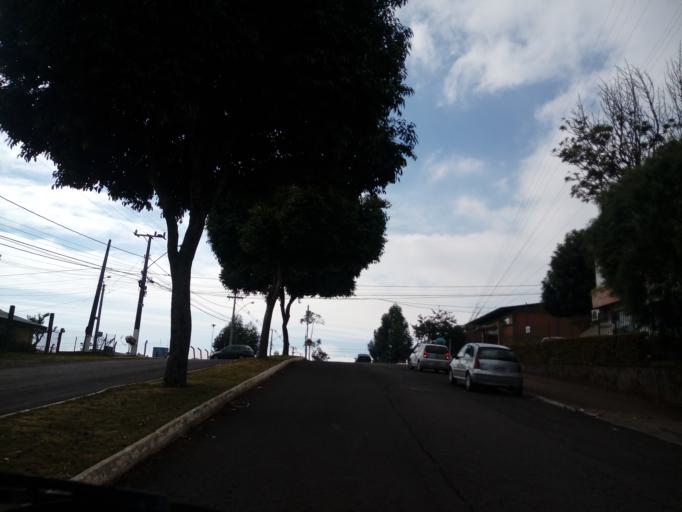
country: BR
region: Santa Catarina
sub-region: Chapeco
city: Chapeco
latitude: -27.0912
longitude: -52.5983
